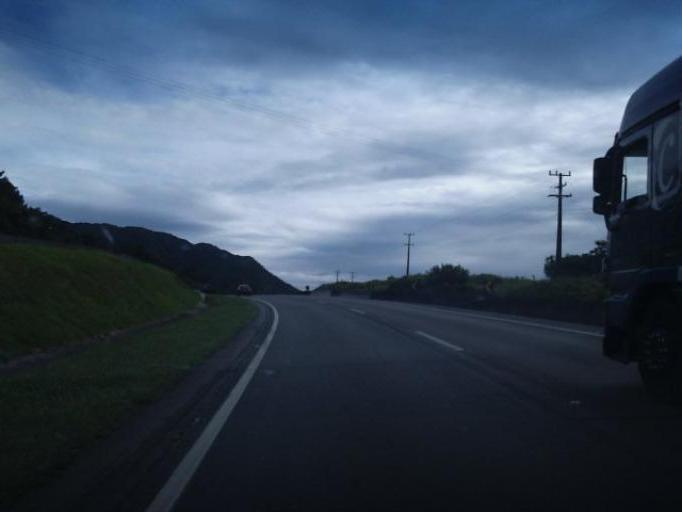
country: BR
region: Parana
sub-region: Campina Grande Do Sul
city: Campina Grande do Sul
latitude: -25.1547
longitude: -48.8614
